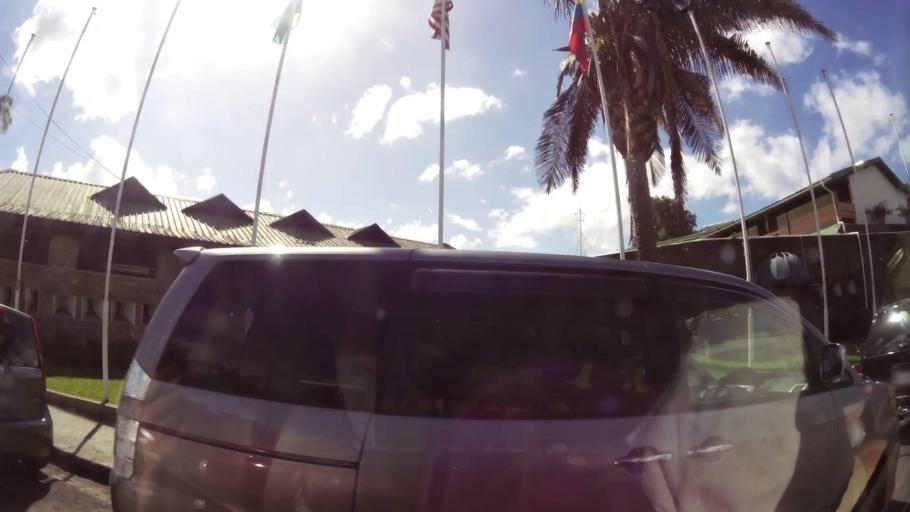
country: DM
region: Saint George
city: Roseau
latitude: 15.2960
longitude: -61.3862
